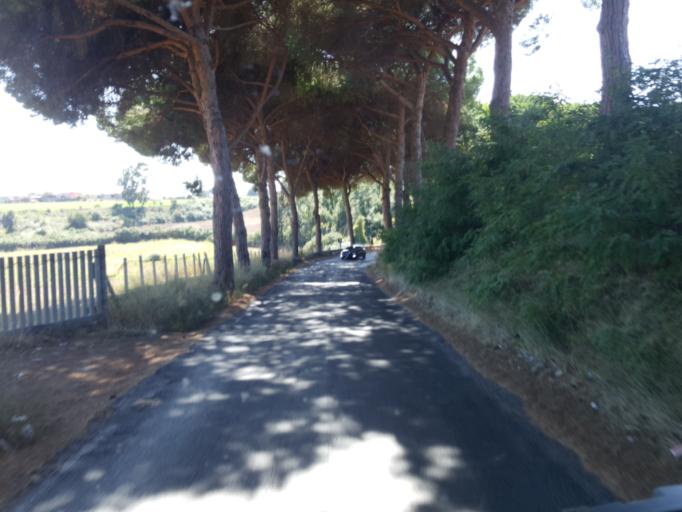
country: IT
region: Latium
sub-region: Citta metropolitana di Roma Capitale
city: Nettuno
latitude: 41.5112
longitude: 12.6519
